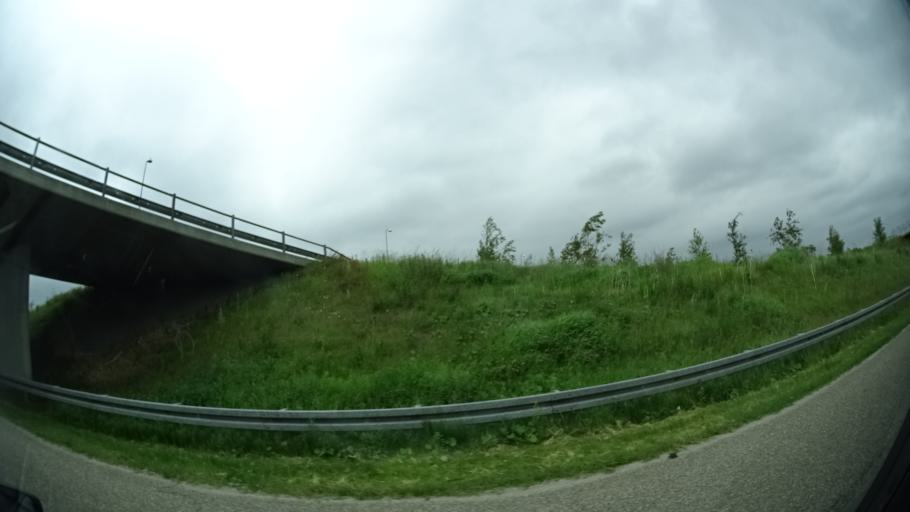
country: DK
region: Central Jutland
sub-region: Arhus Kommune
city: Lystrup
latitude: 56.2235
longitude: 10.2341
